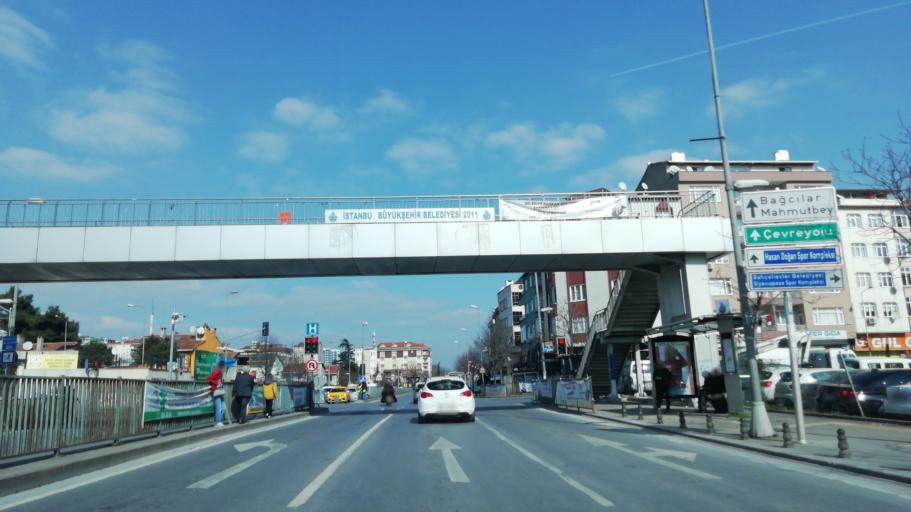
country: TR
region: Istanbul
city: Bahcelievler
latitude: 41.0060
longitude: 28.8470
